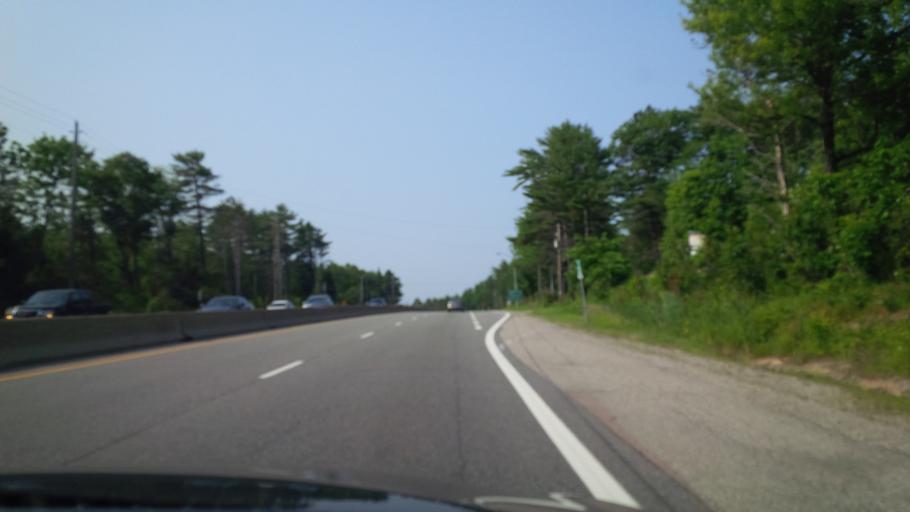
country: CA
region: Ontario
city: Gravenhurst
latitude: 44.8138
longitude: -79.3247
